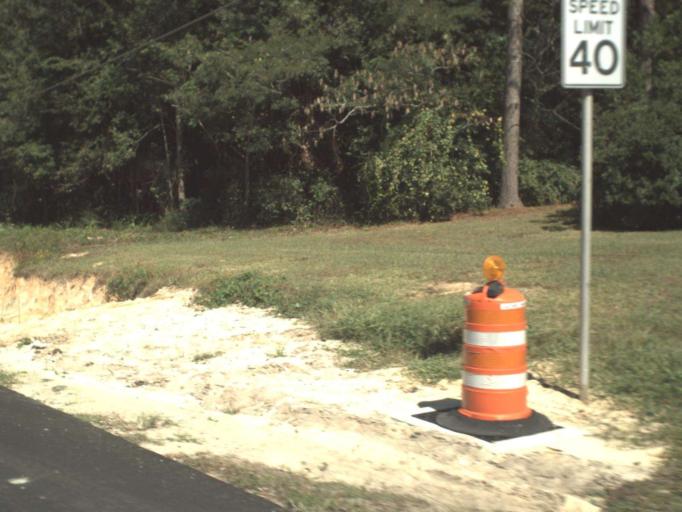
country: US
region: Alabama
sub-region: Covington County
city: Florala
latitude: 30.9846
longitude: -86.3088
